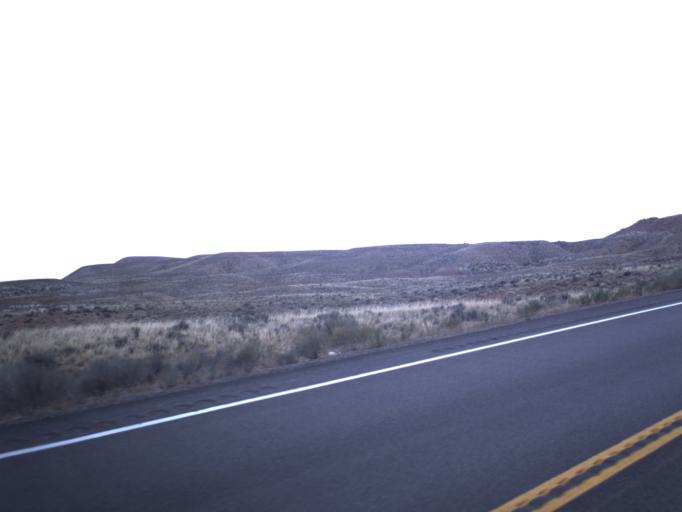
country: US
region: Utah
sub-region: Uintah County
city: Naples
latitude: 40.3007
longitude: -109.4772
